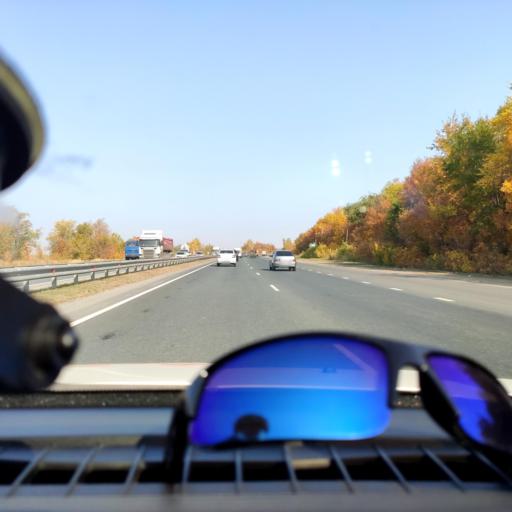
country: RU
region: Samara
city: Novokuybyshevsk
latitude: 52.9986
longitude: 49.9577
